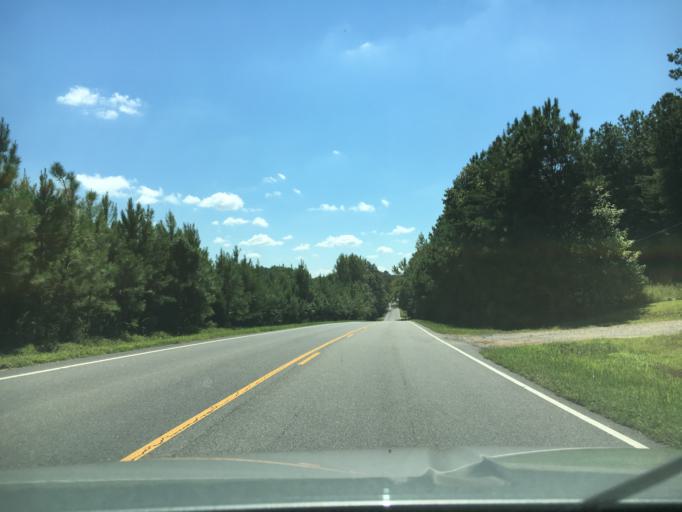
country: US
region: Virginia
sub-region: Amelia County
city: Amelia Court House
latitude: 37.4075
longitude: -77.8934
